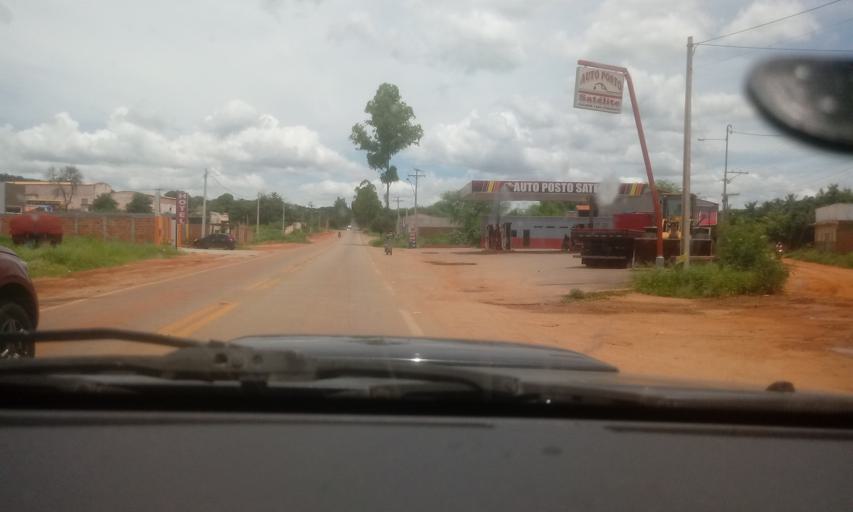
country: BR
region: Bahia
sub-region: Riacho De Santana
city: Riacho de Santana
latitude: -13.6033
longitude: -42.9395
